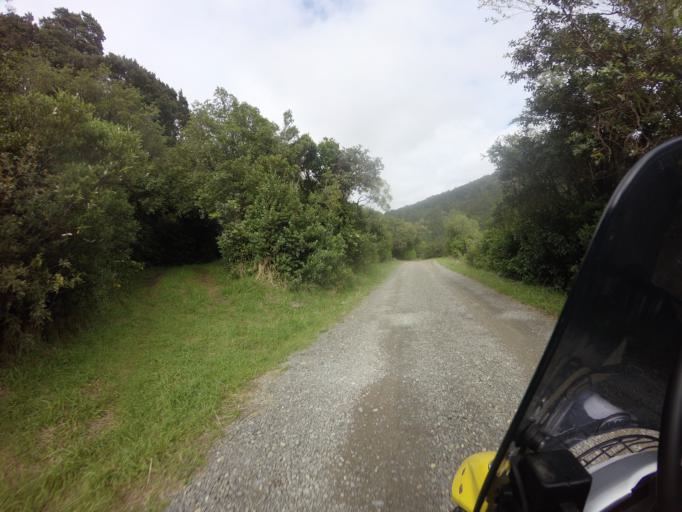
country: NZ
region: Hawke's Bay
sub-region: Wairoa District
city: Wairoa
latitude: -38.7979
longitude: 177.1209
